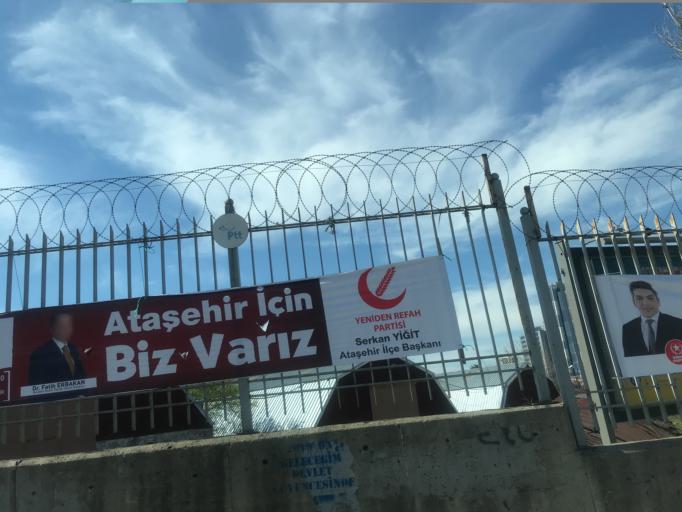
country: TR
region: Istanbul
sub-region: Atasehir
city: Atasehir
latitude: 40.9715
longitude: 29.1083
